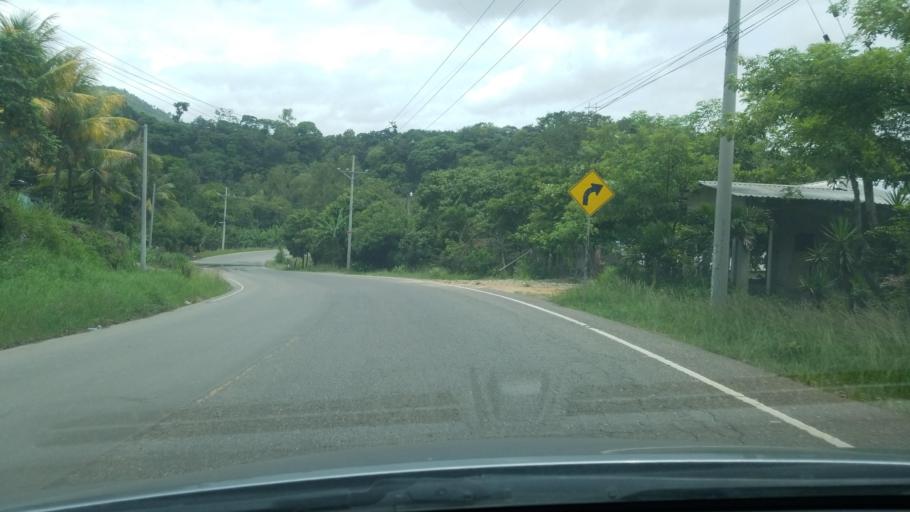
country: HN
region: Copan
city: Cucuyagua
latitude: 14.6705
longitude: -88.8412
